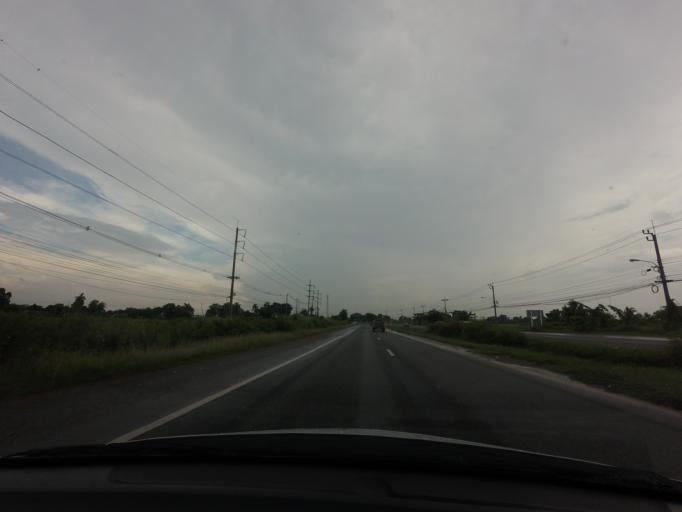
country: TH
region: Bangkok
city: Nong Chok
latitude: 13.8090
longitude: 100.9050
